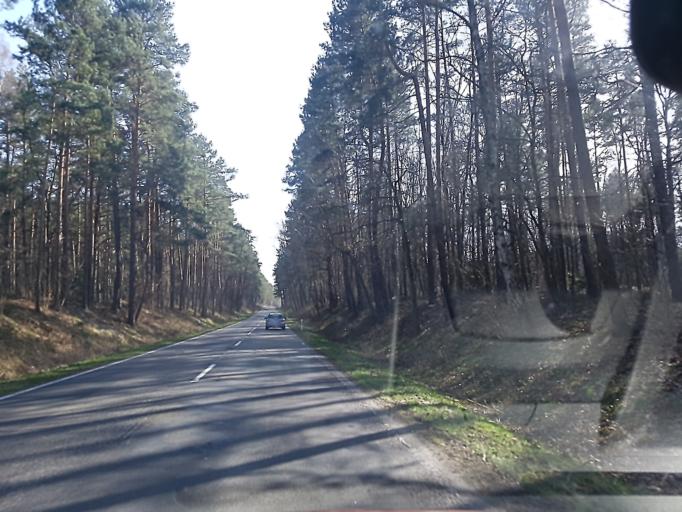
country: DE
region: Brandenburg
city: Bronkow
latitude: 51.7102
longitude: 13.9205
